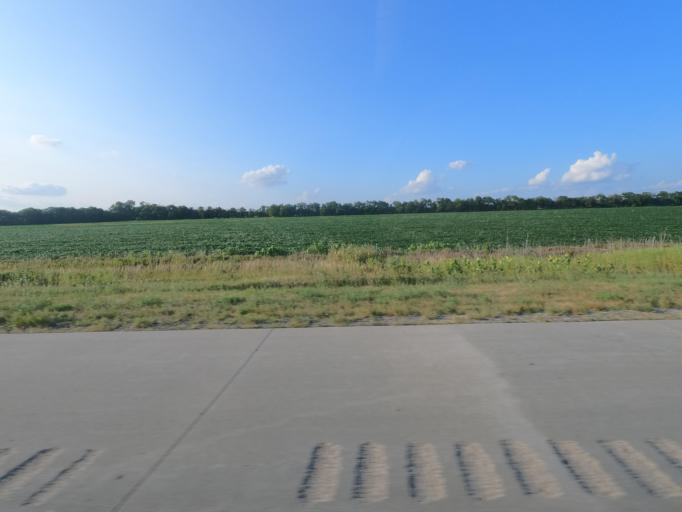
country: US
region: Kansas
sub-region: Dickinson County
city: Solomon
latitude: 38.9082
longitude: -97.4348
